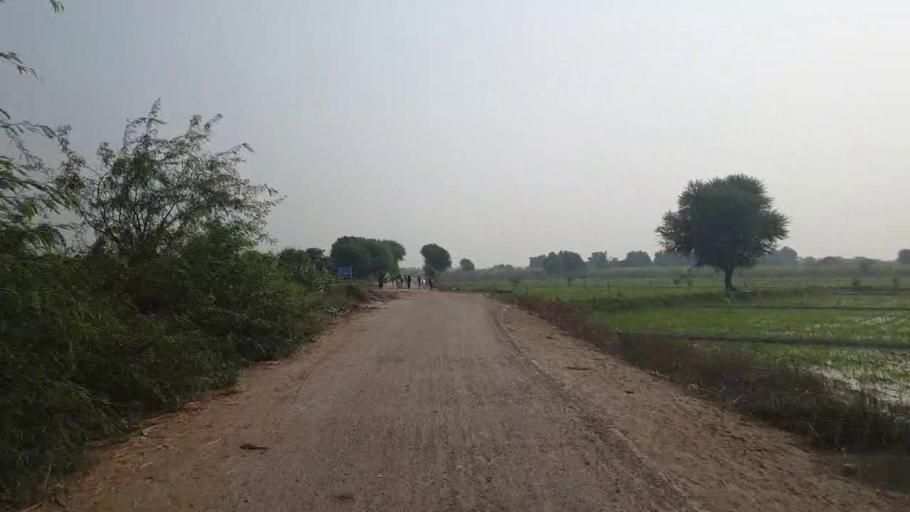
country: PK
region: Sindh
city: Tando Muhammad Khan
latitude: 25.2457
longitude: 68.5635
